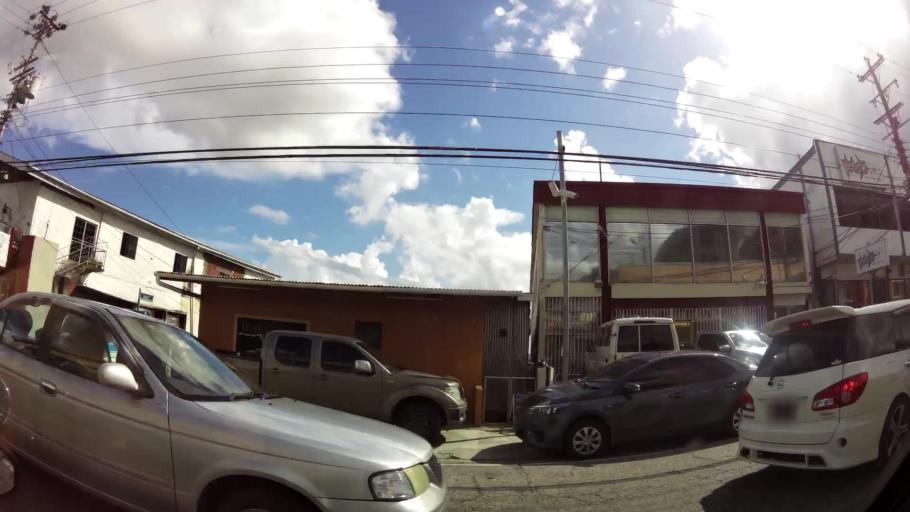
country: TT
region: City of San Fernando
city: Mon Repos
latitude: 10.2776
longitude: -61.4564
